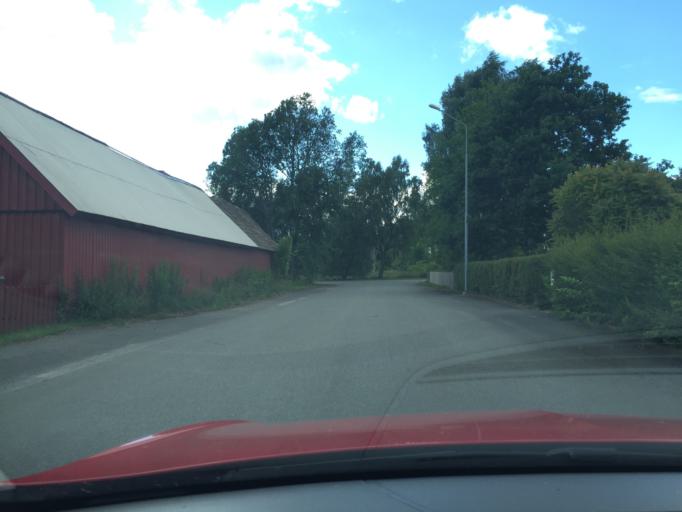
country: SE
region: Skane
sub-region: Hassleholms Kommun
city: Sosdala
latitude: 56.0357
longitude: 13.6748
